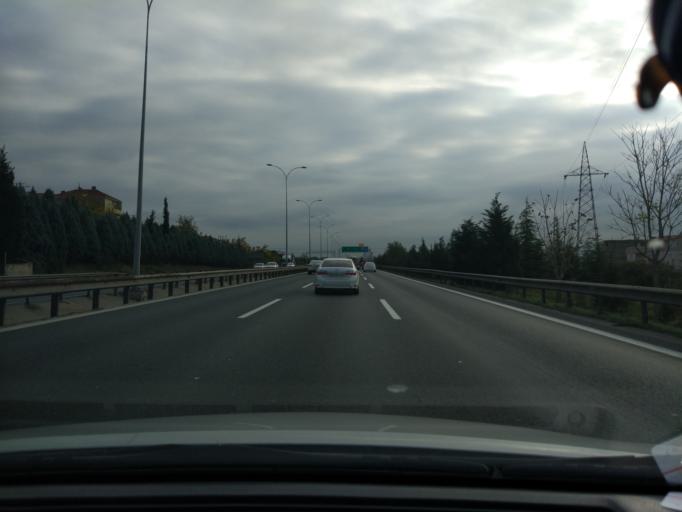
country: TR
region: Kocaeli
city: Korfez
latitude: 40.7744
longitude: 29.7615
